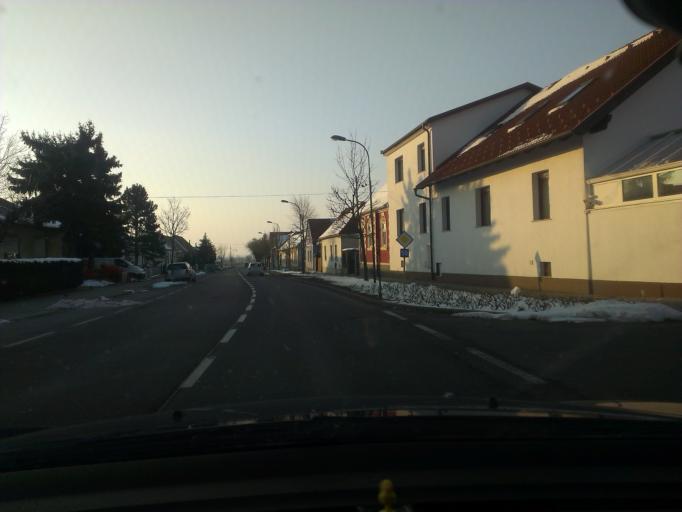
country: AT
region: Burgenland
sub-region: Eisenstadt-Umgebung
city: Donnerskirchen
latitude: 47.8932
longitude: 16.6473
